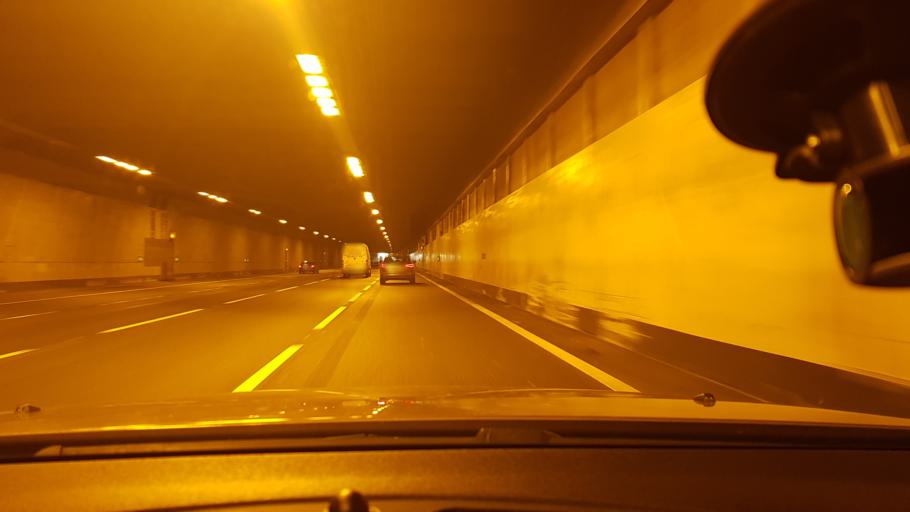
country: GB
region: England
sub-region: Hertfordshire
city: Waltham Cross
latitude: 51.6828
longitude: -0.0411
